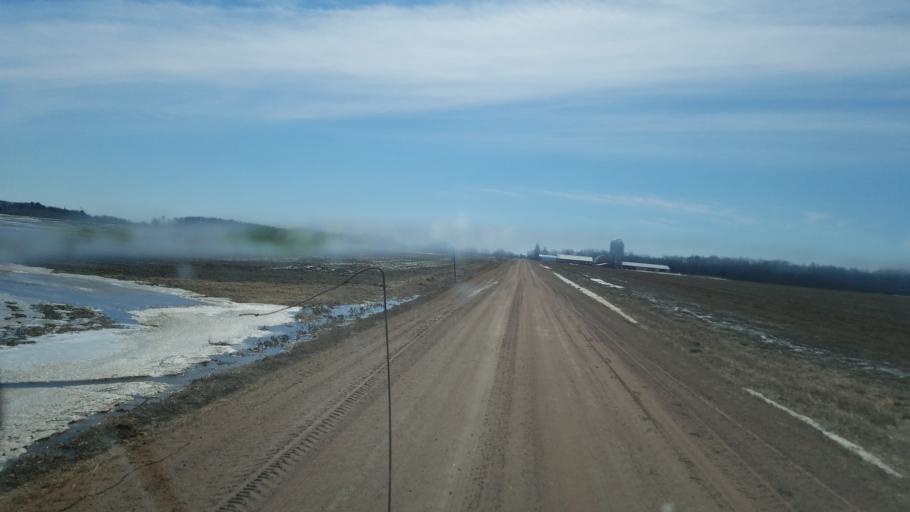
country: US
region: Wisconsin
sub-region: Clark County
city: Loyal
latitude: 44.6386
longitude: -90.4075
